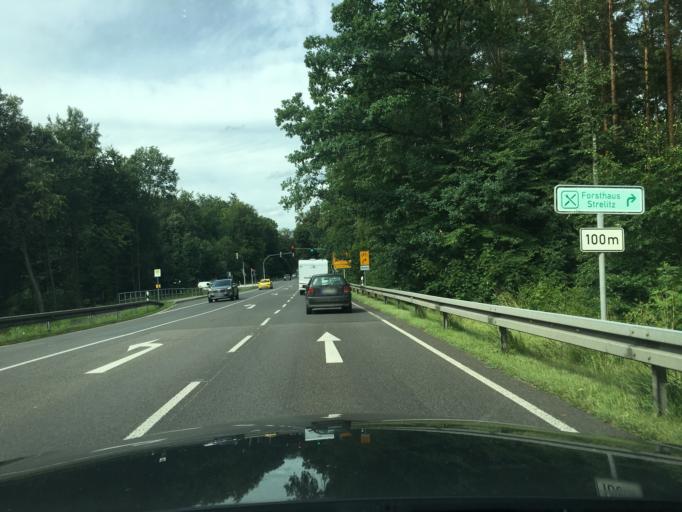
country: DE
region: Mecklenburg-Vorpommern
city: Neustrelitz
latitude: 53.3034
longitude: 13.1048
